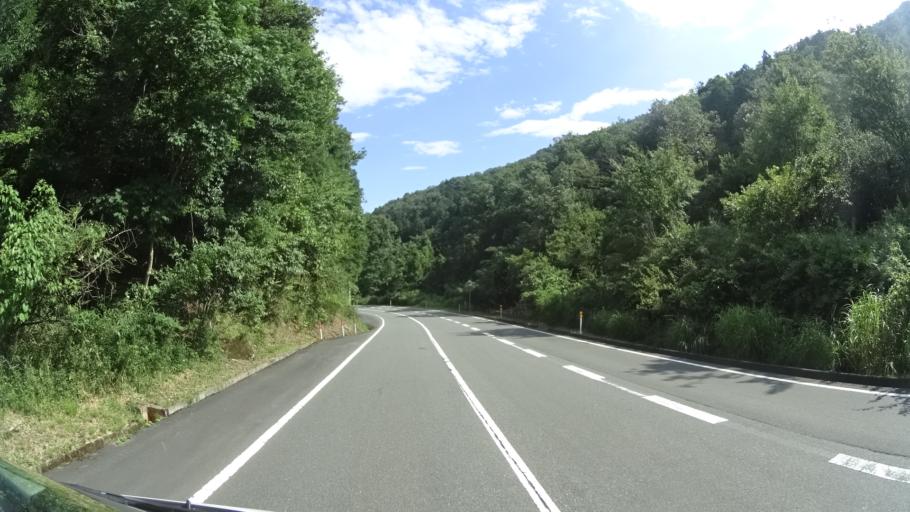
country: JP
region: Kyoto
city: Fukuchiyama
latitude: 35.3437
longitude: 135.1591
